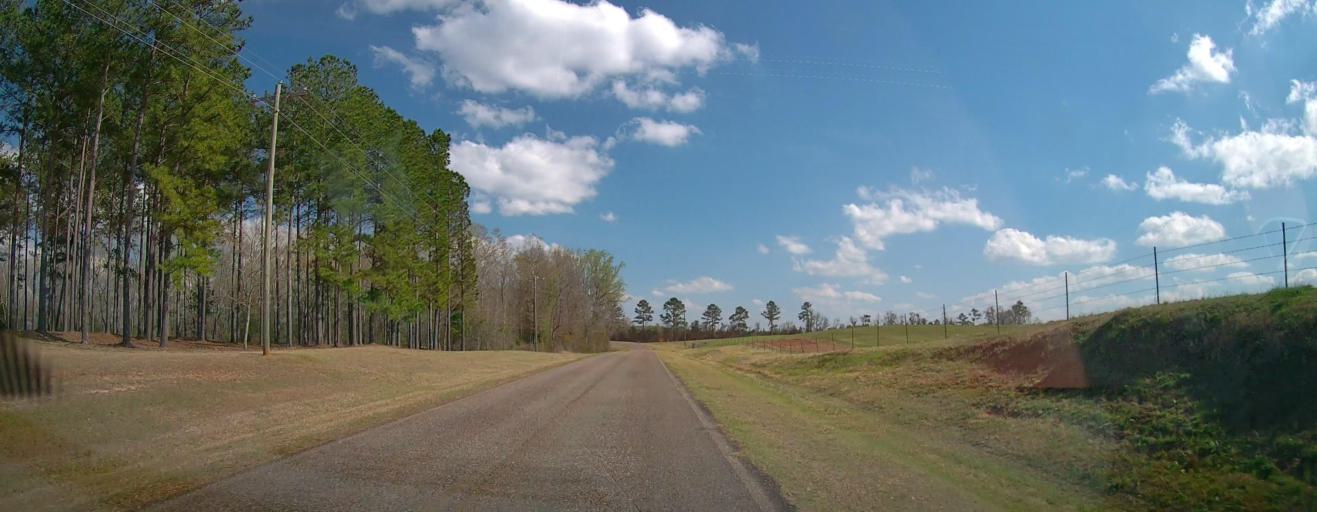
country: US
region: Georgia
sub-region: Twiggs County
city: Jeffersonville
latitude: 32.6514
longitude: -83.2020
